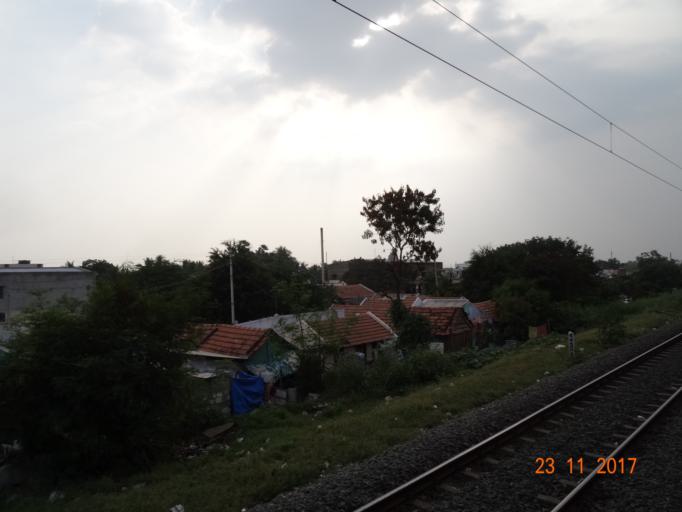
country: IN
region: Tamil Nadu
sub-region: Tiruppur
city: Tiruppur
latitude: 11.1082
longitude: 77.3149
